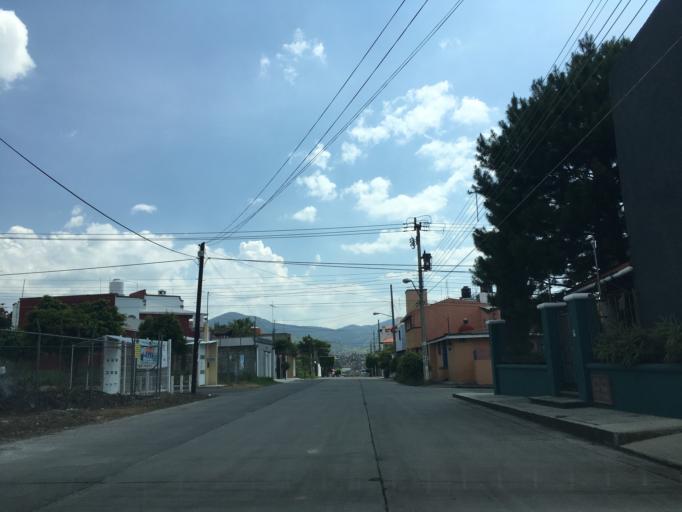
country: MX
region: Michoacan
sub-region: Morelia
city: Montana Monarca (Punta Altozano)
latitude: 19.6741
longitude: -101.1837
